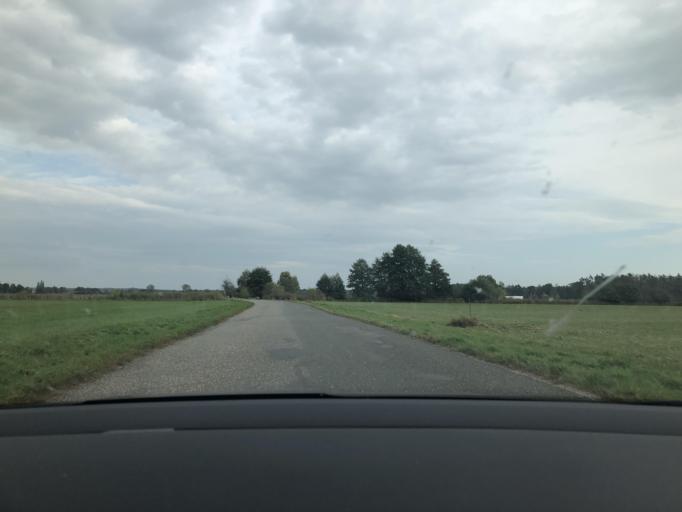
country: CZ
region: Pardubicky
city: Recany nad Labem
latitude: 50.0791
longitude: 15.4509
